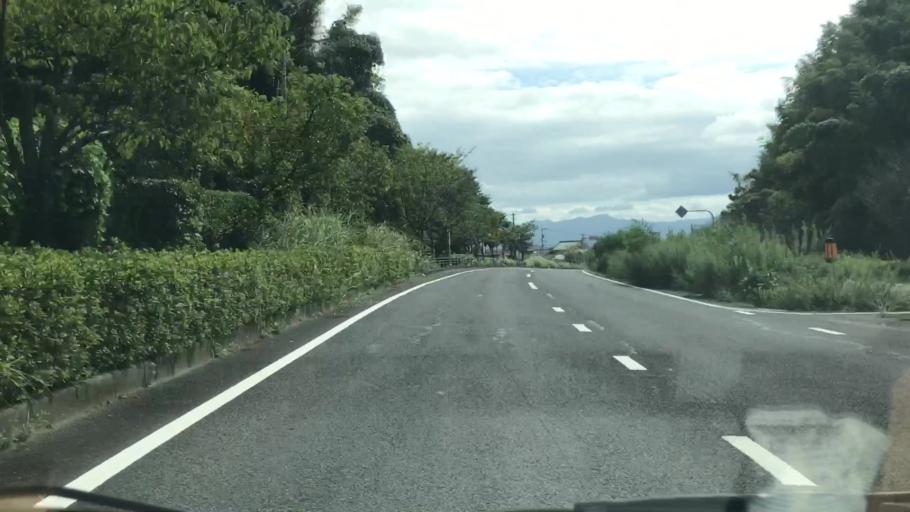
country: JP
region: Saga Prefecture
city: Saga-shi
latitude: 33.2285
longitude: 130.1801
